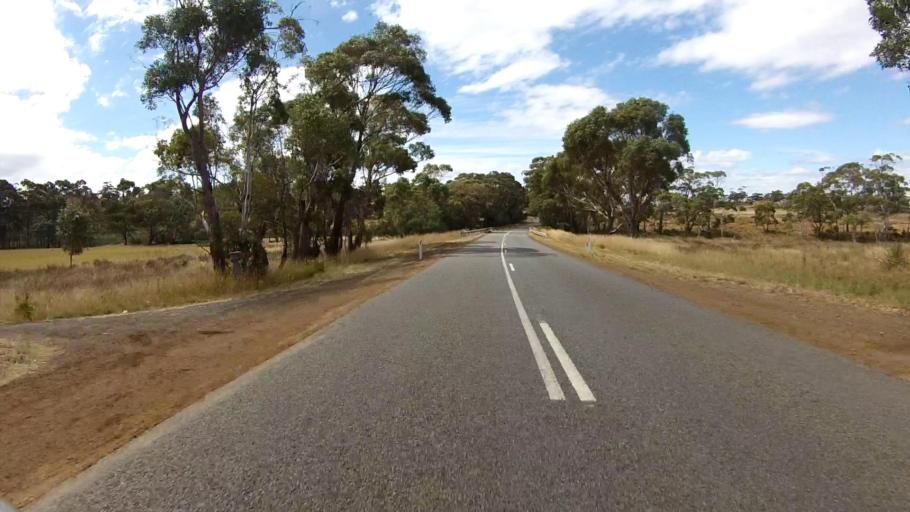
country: AU
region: Tasmania
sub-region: Sorell
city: Sorell
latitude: -42.3059
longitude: 147.9657
